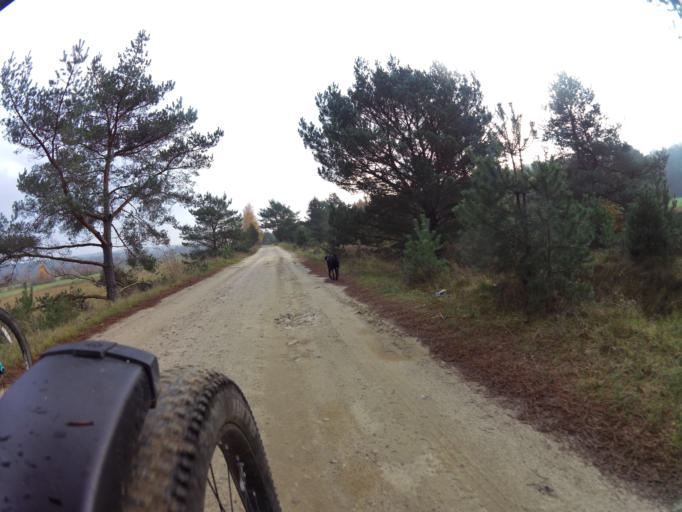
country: PL
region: Pomeranian Voivodeship
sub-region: Powiat wejherowski
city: Gniewino
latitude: 54.7052
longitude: 18.1040
